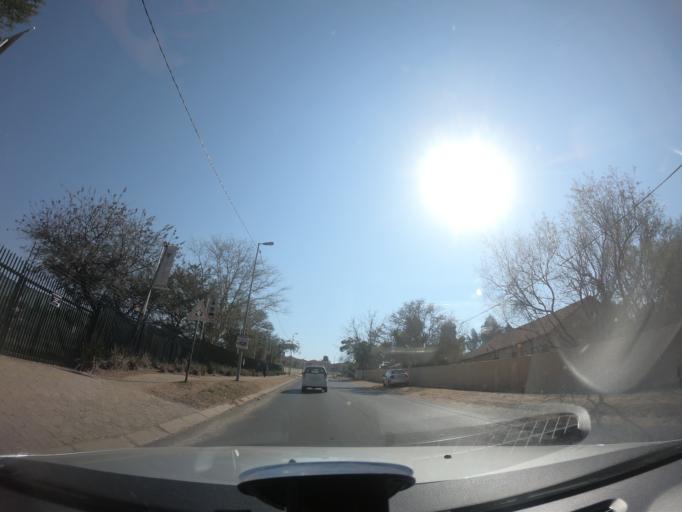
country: ZA
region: Gauteng
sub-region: City of Johannesburg Metropolitan Municipality
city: Diepsloot
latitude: -26.0170
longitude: 27.9965
